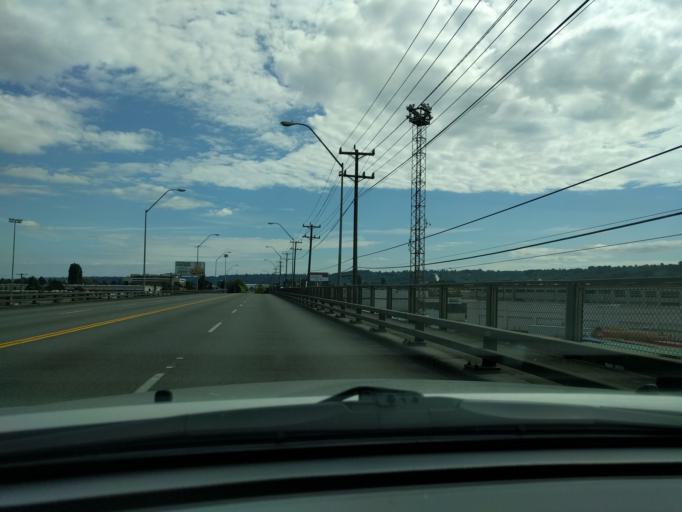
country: US
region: Washington
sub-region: King County
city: Seattle
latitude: 47.5599
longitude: -122.3295
